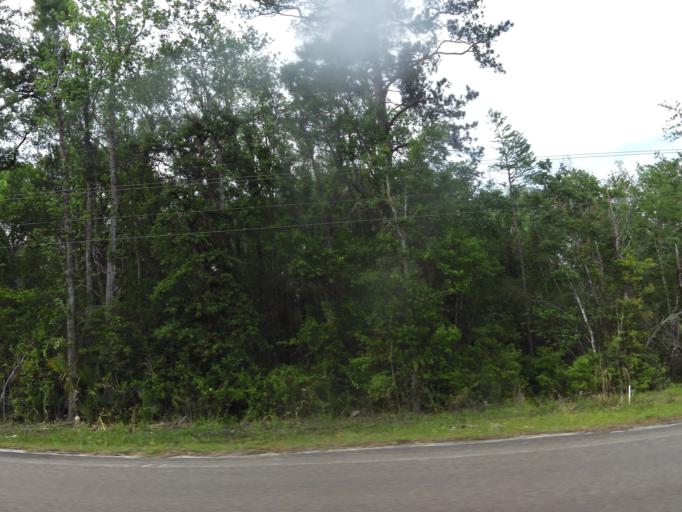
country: US
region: Georgia
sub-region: Camden County
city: Kingsland
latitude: 30.7000
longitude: -81.7606
